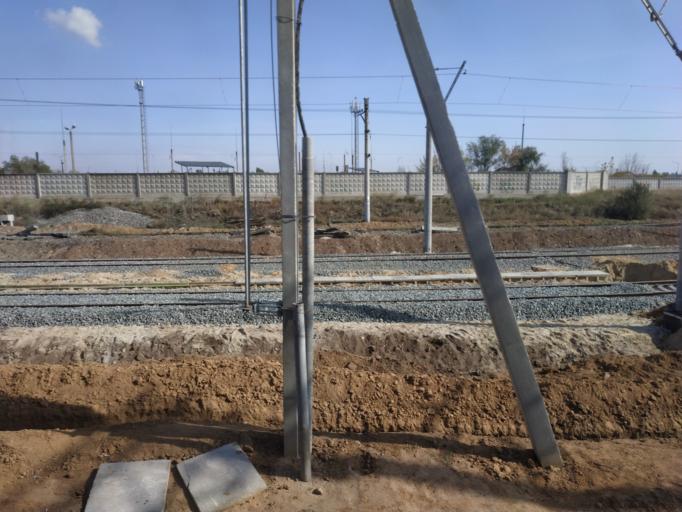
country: RU
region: Volgograd
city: Gumrak
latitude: 48.7740
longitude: 44.3831
